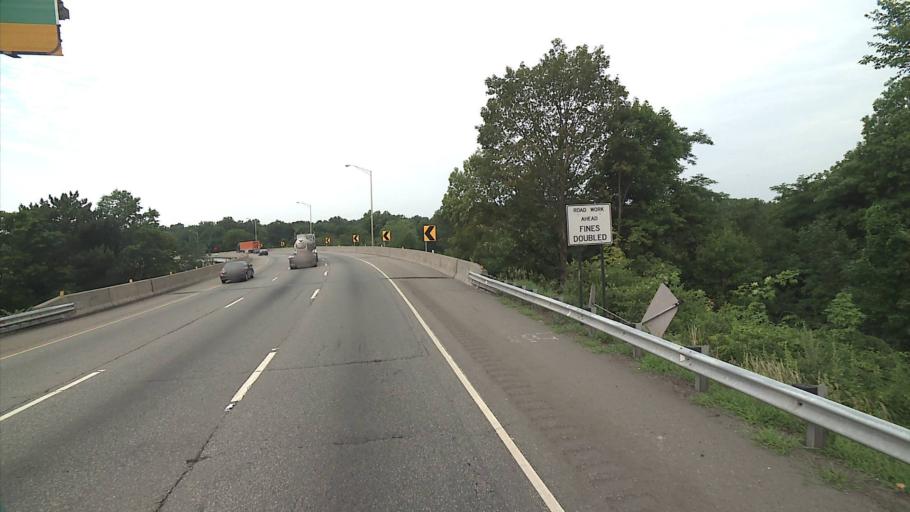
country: US
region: Connecticut
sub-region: Hartford County
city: West Hartford
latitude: 41.7491
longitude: -72.7334
